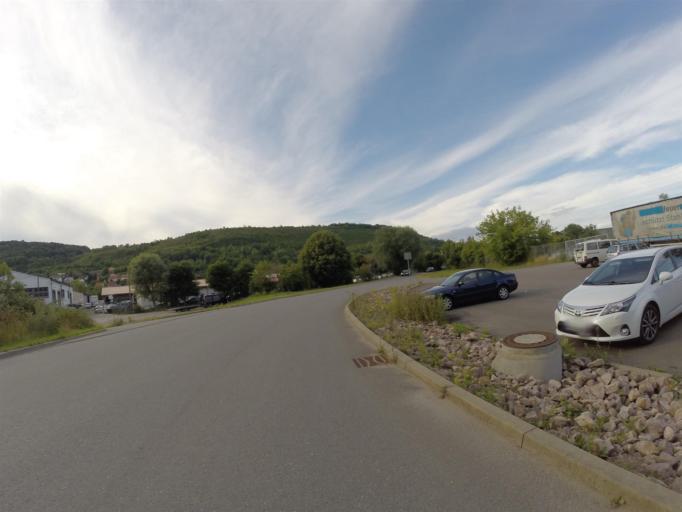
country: DE
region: Thuringia
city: Neuengonna
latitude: 50.9756
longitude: 11.6498
